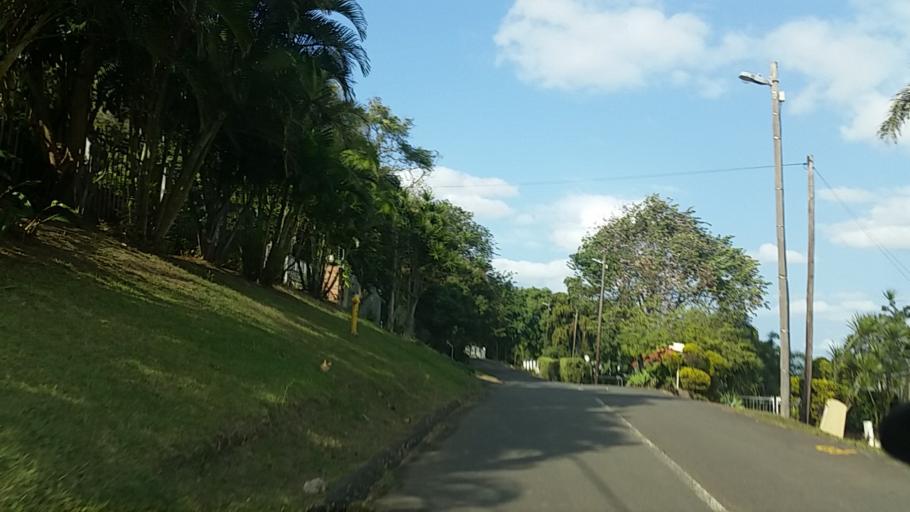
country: ZA
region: KwaZulu-Natal
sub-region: eThekwini Metropolitan Municipality
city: Berea
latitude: -29.8305
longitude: 30.9586
